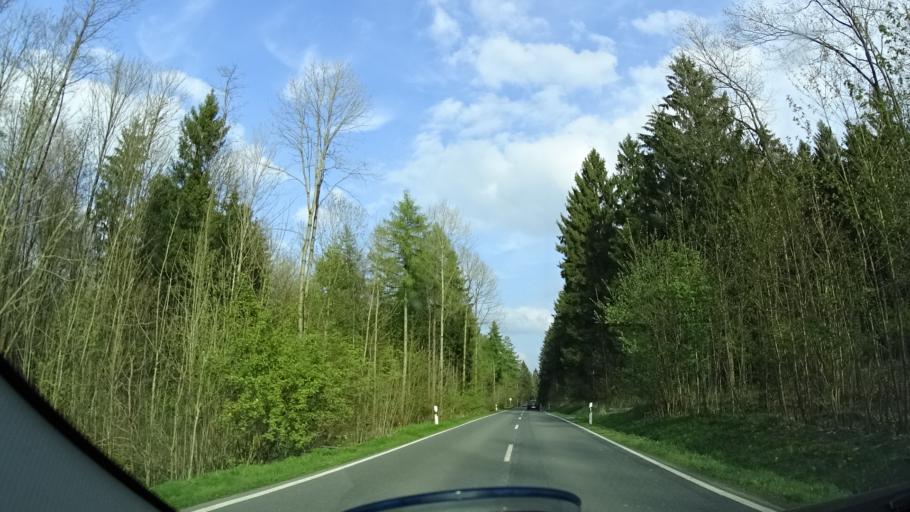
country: DE
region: North Rhine-Westphalia
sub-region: Regierungsbezirk Detmold
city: Buren
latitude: 51.5613
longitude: 8.6346
